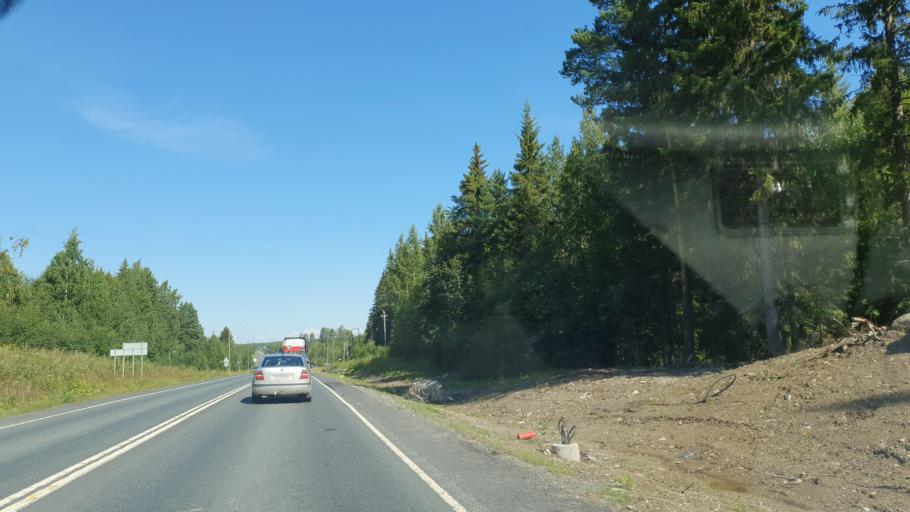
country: FI
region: Northern Savo
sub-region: Ylae-Savo
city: Lapinlahti
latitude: 63.3057
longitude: 27.4502
